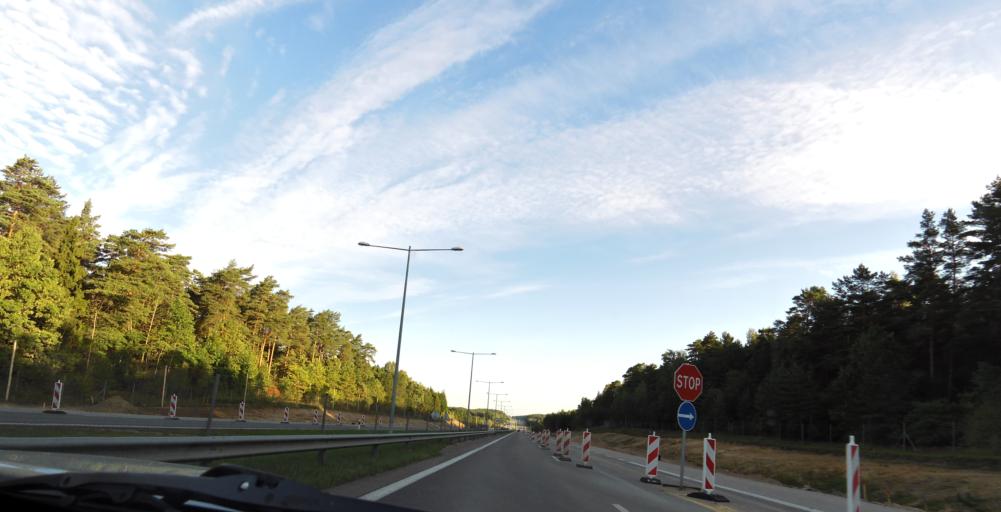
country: LT
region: Vilnius County
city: Ukmerge
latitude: 55.2482
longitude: 24.8188
